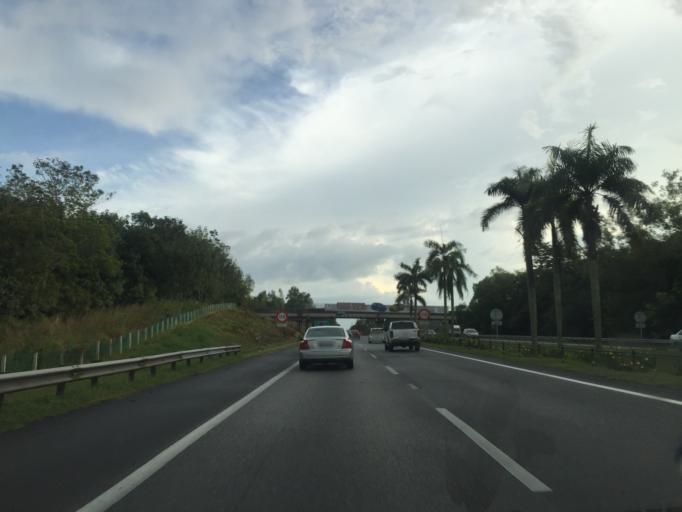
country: MY
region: Kedah
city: Gurun
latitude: 5.8415
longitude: 100.4864
